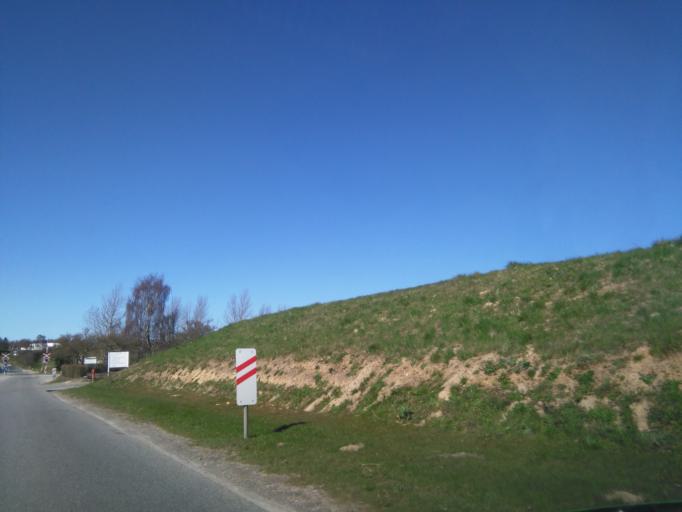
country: DK
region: Central Jutland
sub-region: Arhus Kommune
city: Tranbjerg
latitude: 56.1078
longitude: 10.1276
